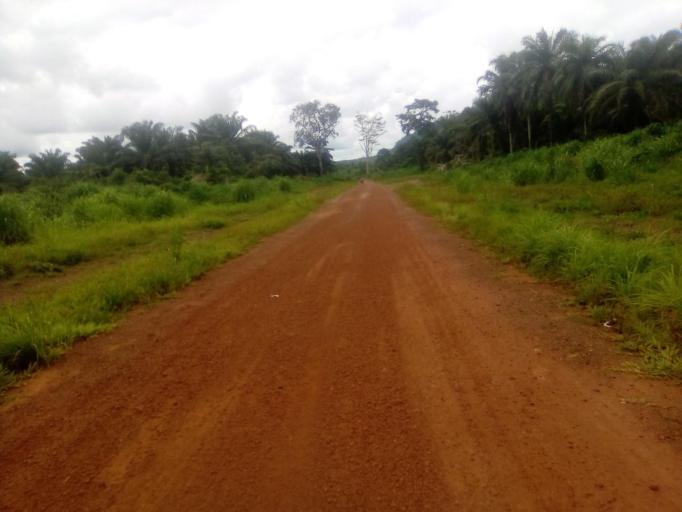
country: SL
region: Southern Province
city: Moyamba
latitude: 8.1411
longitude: -12.4409
